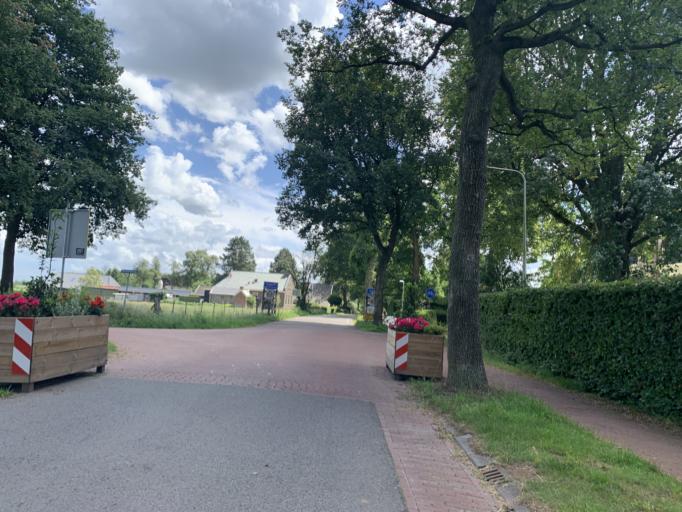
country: NL
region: Groningen
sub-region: Gemeente Haren
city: Haren
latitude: 53.1545
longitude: 6.6429
